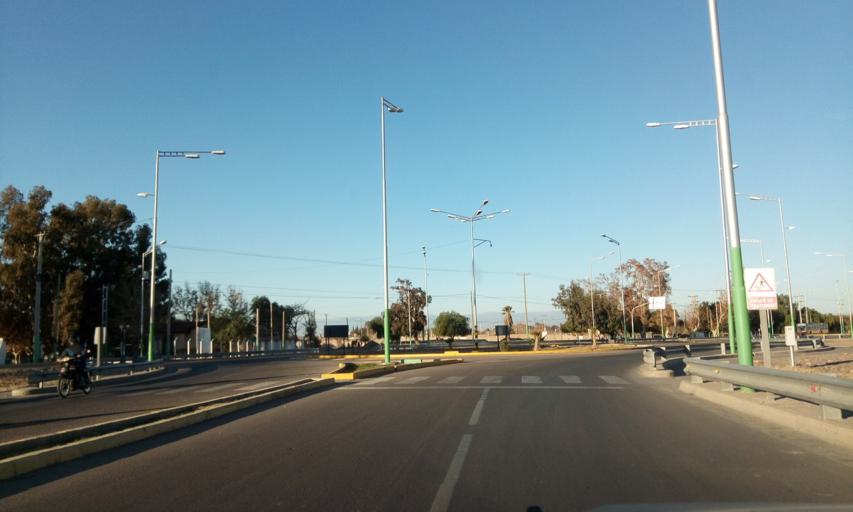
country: AR
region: San Juan
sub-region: Departamento de Rivadavia
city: Rivadavia
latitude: -31.5230
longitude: -68.6184
